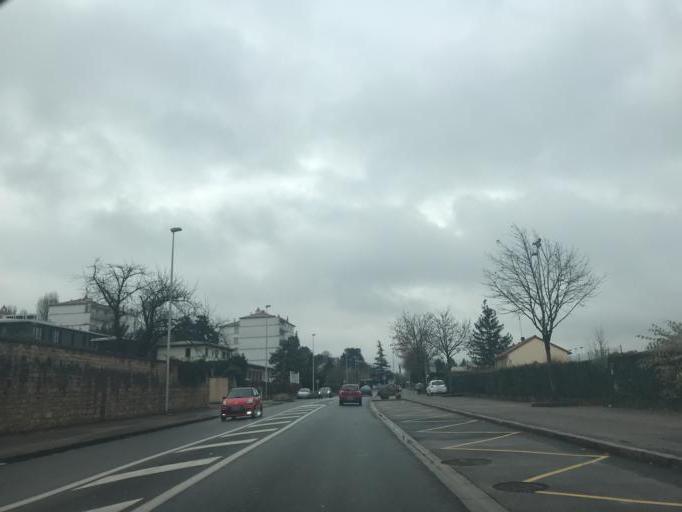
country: FR
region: Rhone-Alpes
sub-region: Departement du Rhone
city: Albigny-sur-Saone
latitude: 45.8705
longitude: 4.8398
